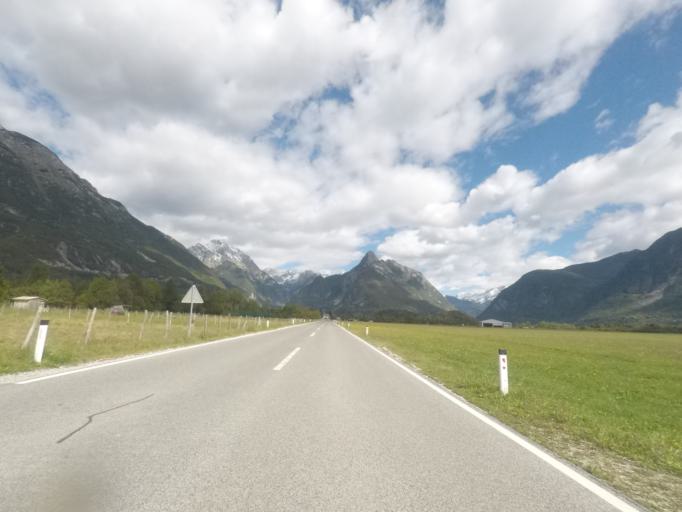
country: SI
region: Bovec
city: Bovec
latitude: 46.3305
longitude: 13.5461
